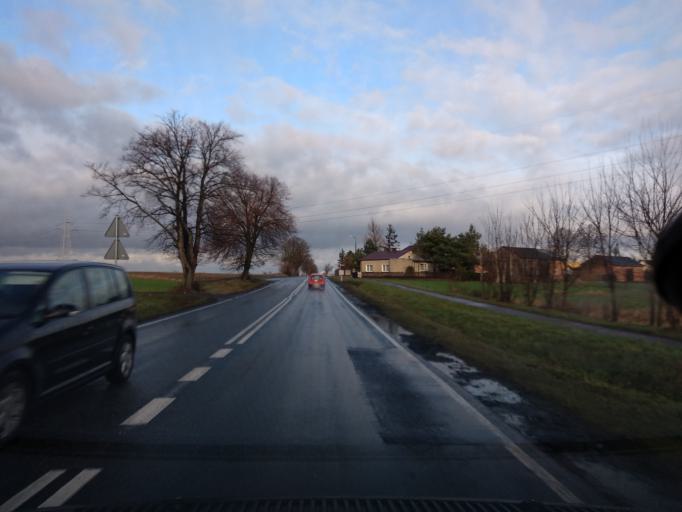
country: PL
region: Greater Poland Voivodeship
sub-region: Powiat koninski
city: Rychwal
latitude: 52.0803
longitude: 18.1610
